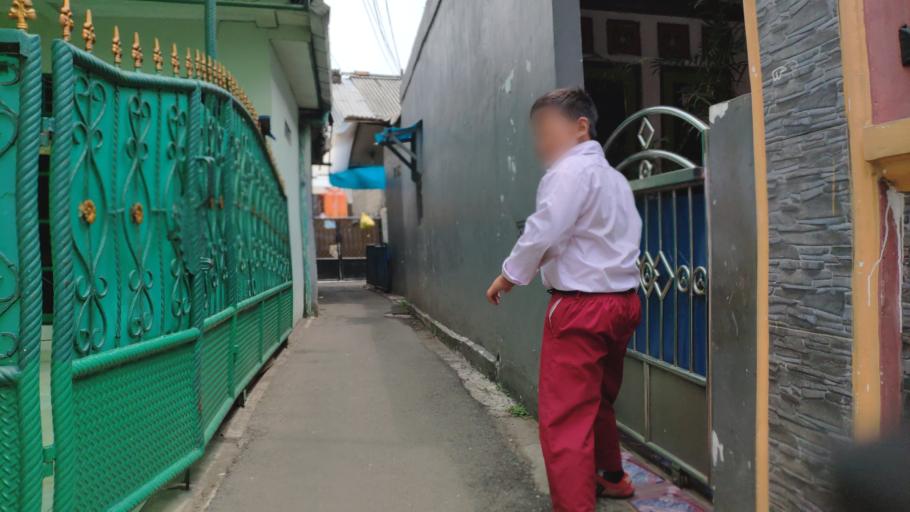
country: ID
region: West Java
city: Depok
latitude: -6.3179
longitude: 106.8344
